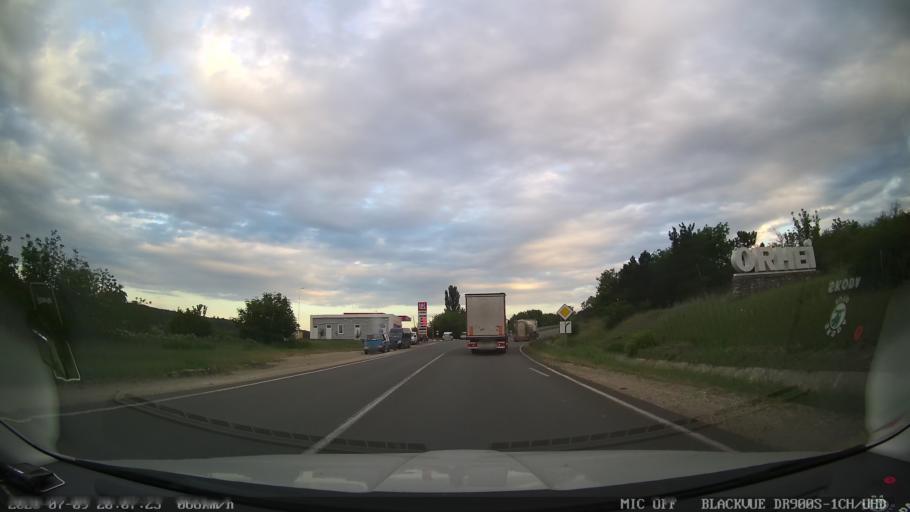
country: MD
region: Orhei
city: Orhei
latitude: 47.4057
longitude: 28.8169
